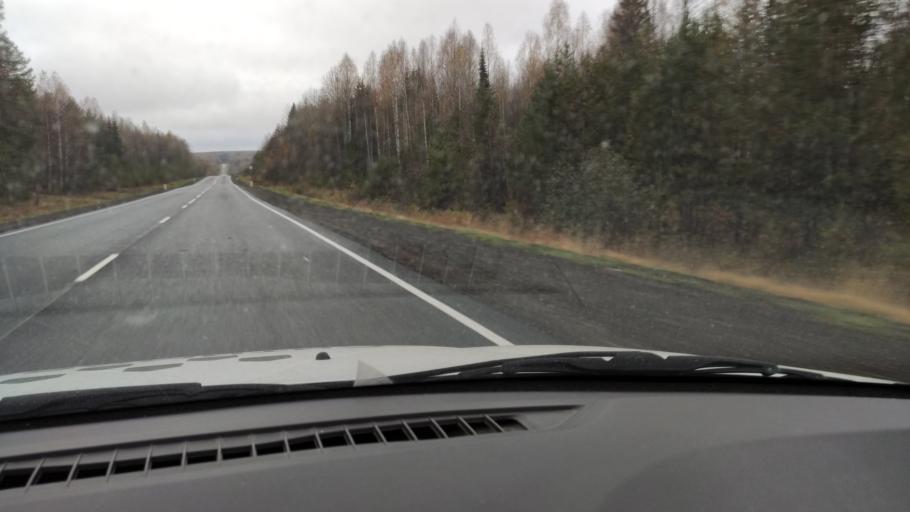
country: RU
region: Kirov
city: Chernaya Kholunitsa
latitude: 58.8876
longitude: 51.3795
